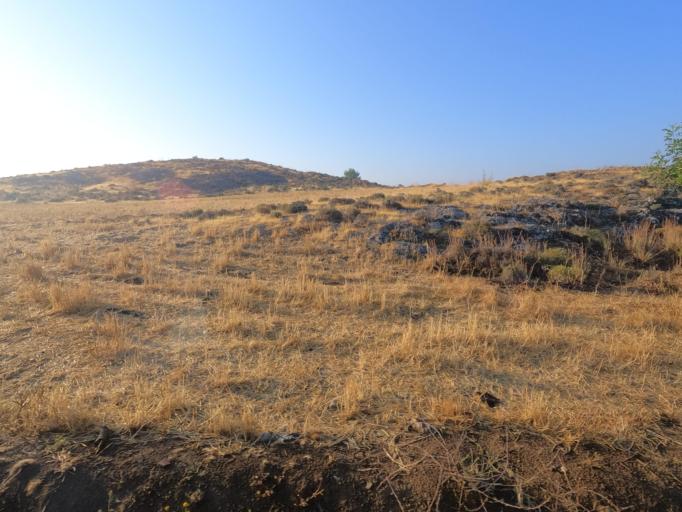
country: CY
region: Larnaka
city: Mosfiloti
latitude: 34.9740
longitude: 33.4326
